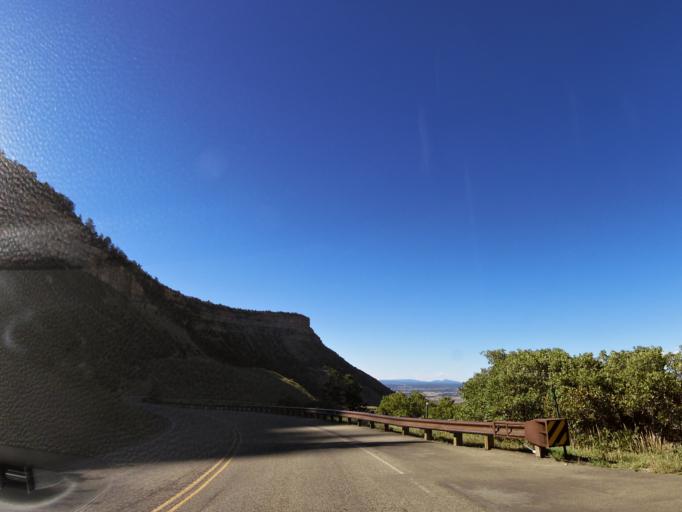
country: US
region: Colorado
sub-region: Montezuma County
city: Mancos
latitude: 37.3045
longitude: -108.4111
